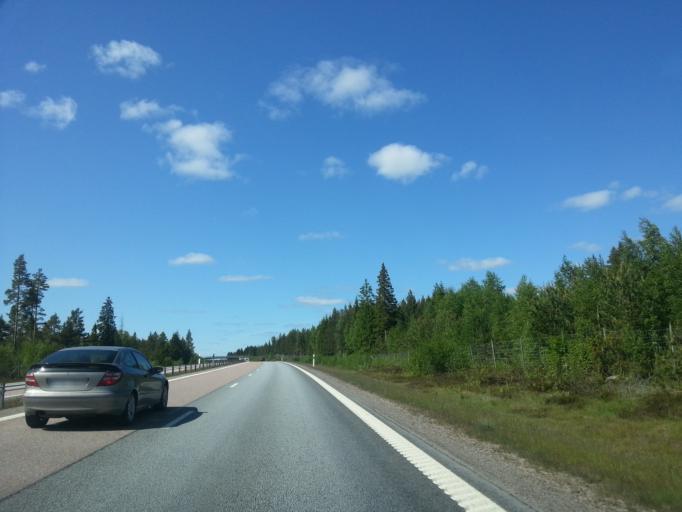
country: SE
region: Gaevleborg
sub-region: Soderhamns Kommun
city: Soderhamn
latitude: 61.3679
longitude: 17.0090
